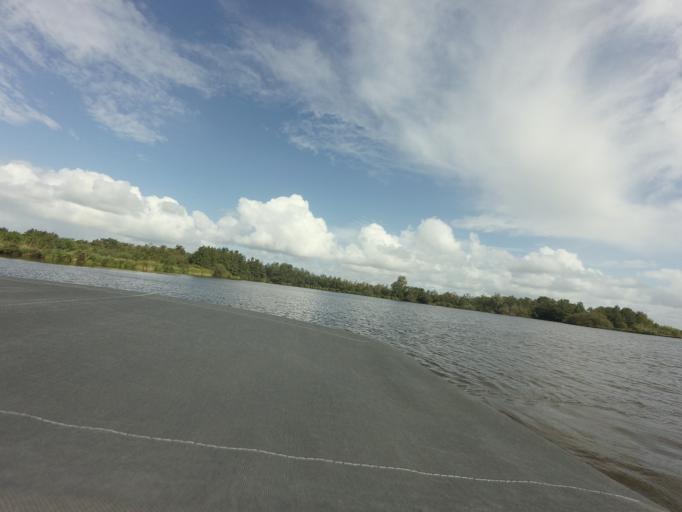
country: NL
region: Friesland
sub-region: Gemeente Boarnsterhim
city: Warten
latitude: 53.1162
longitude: 5.9277
